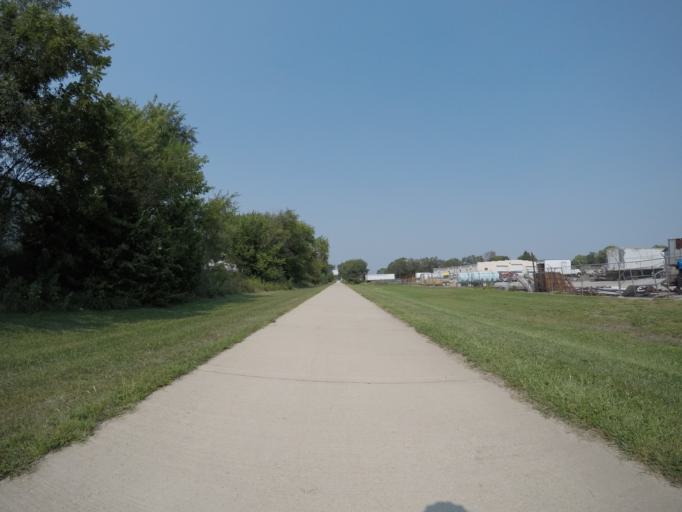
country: US
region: Nebraska
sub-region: Gage County
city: Beatrice
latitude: 40.2576
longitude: -96.7405
